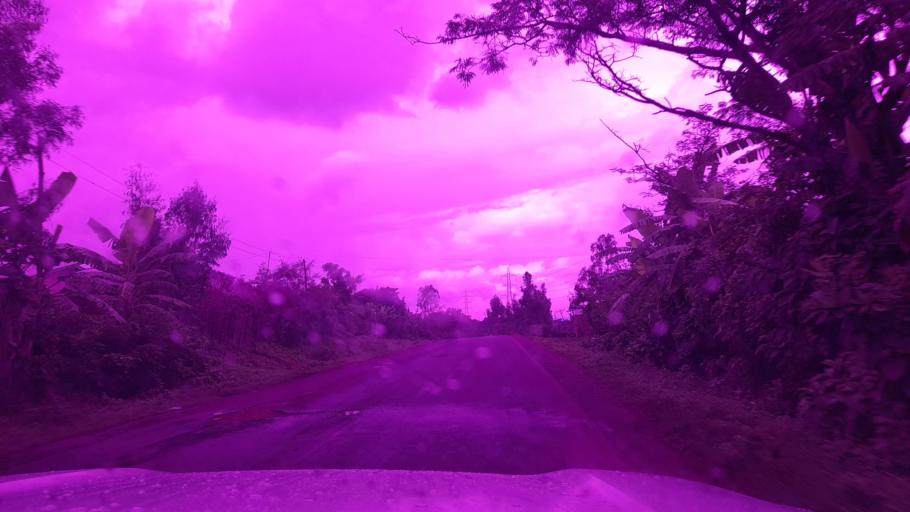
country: ET
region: Oromiya
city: Jima
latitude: 7.7085
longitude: 37.0599
